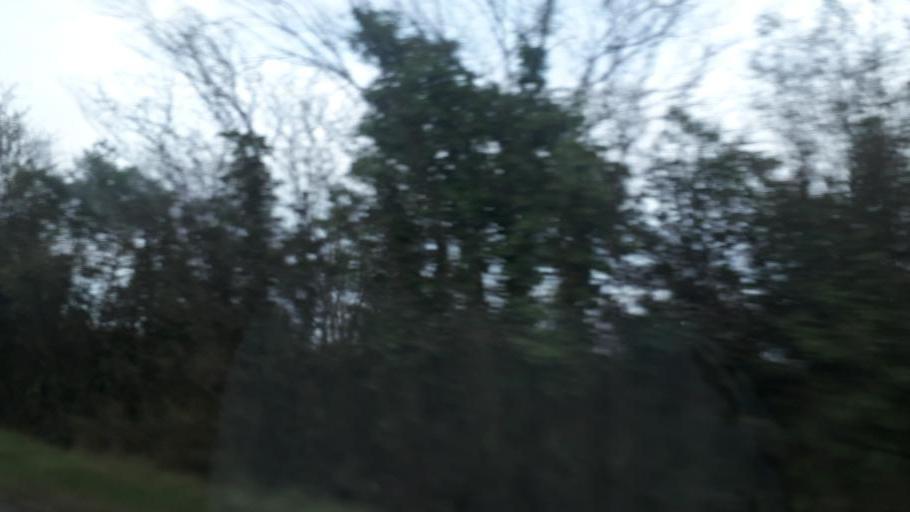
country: IE
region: Leinster
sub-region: Laois
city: Portlaoise
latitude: 52.9821
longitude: -7.3191
